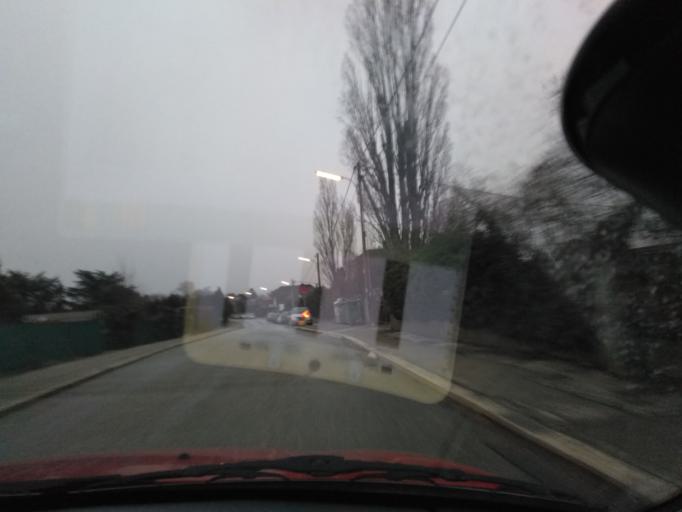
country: AT
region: Vienna
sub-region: Wien Stadt
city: Vienna
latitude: 48.2322
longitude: 16.3069
